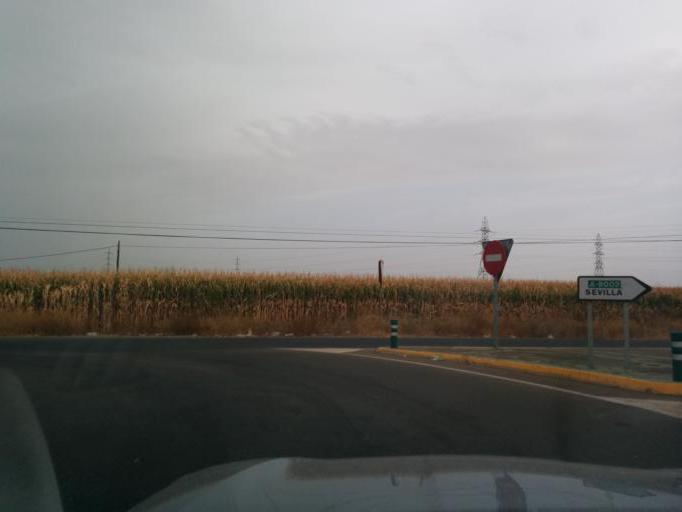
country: ES
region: Andalusia
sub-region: Provincia de Sevilla
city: La Algaba
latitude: 37.4493
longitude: -5.9772
